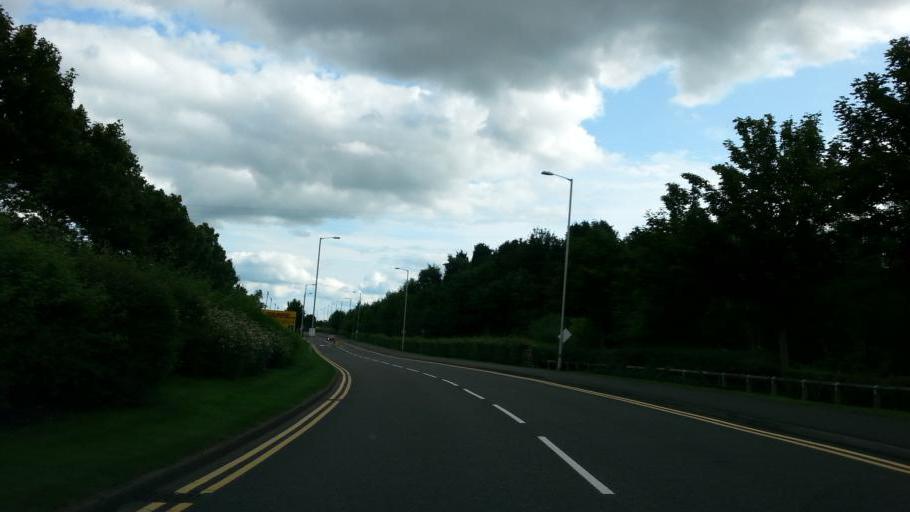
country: GB
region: England
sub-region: Coventry
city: Keresley
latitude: 52.4542
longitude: -1.5318
